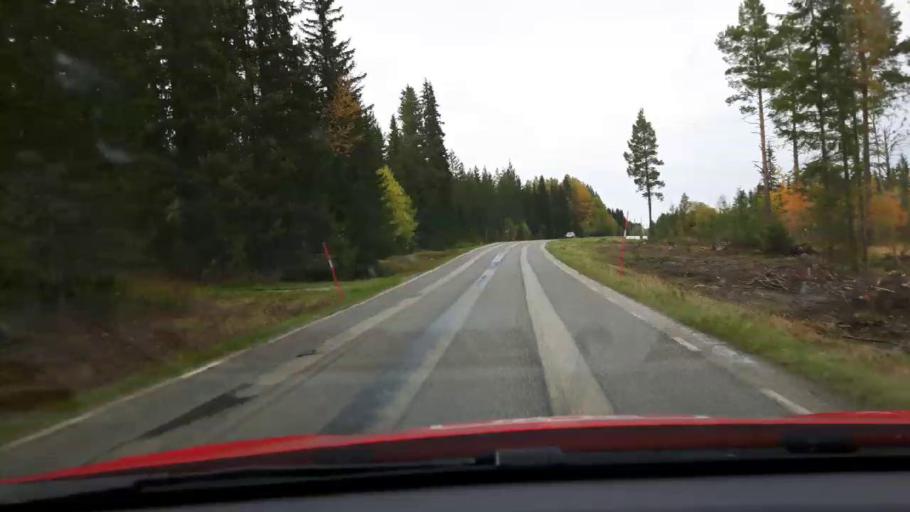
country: SE
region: Jaemtland
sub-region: Bergs Kommun
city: Hoverberg
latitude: 62.8218
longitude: 14.3946
